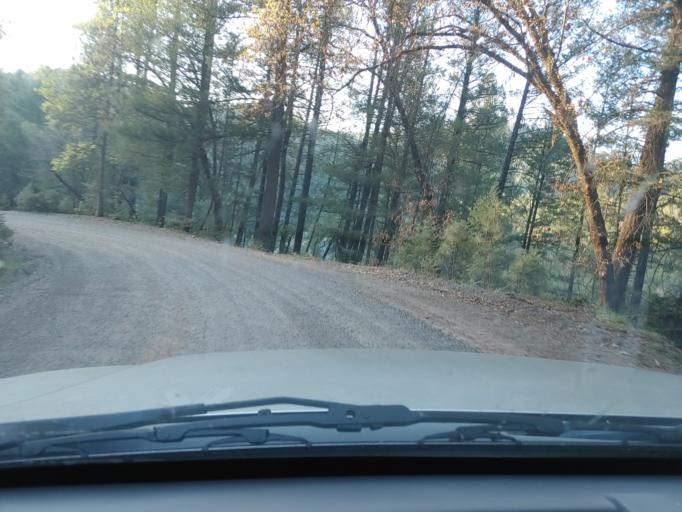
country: US
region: California
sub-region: Shasta County
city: Bella Vista
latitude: 40.8420
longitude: -122.0131
